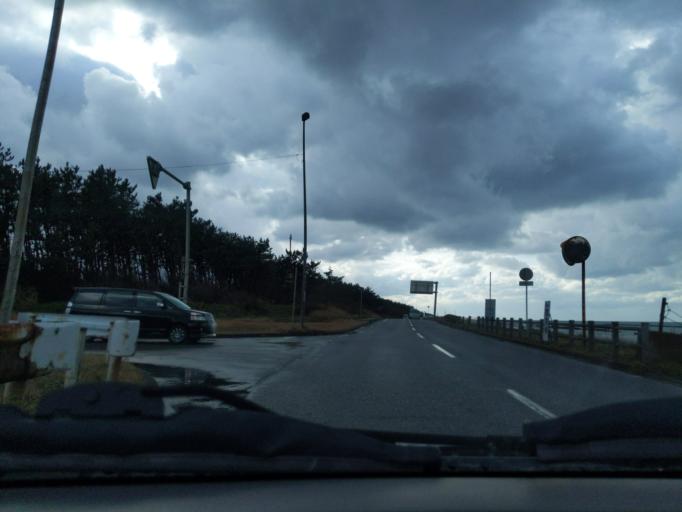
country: JP
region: Niigata
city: Niigata-shi
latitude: 37.9260
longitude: 139.0300
